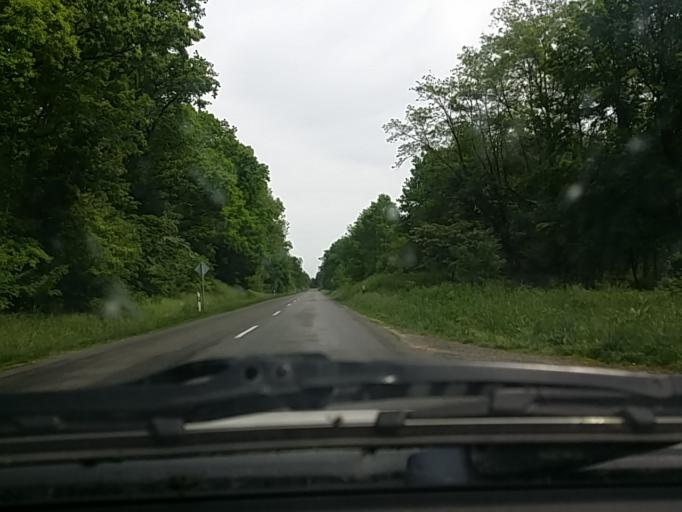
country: HU
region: Somogy
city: Barcs
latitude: 45.9637
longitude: 17.5057
